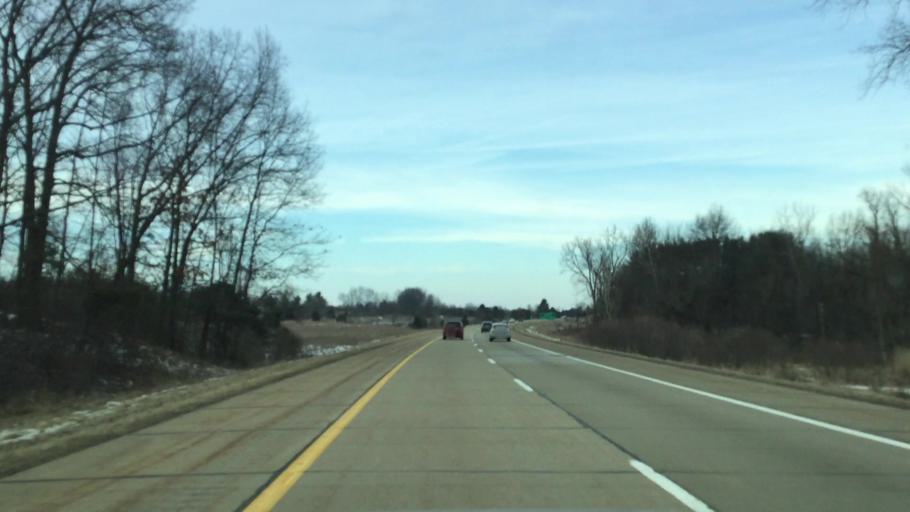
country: US
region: Michigan
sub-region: Eaton County
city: Olivet
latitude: 42.4028
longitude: -84.9688
